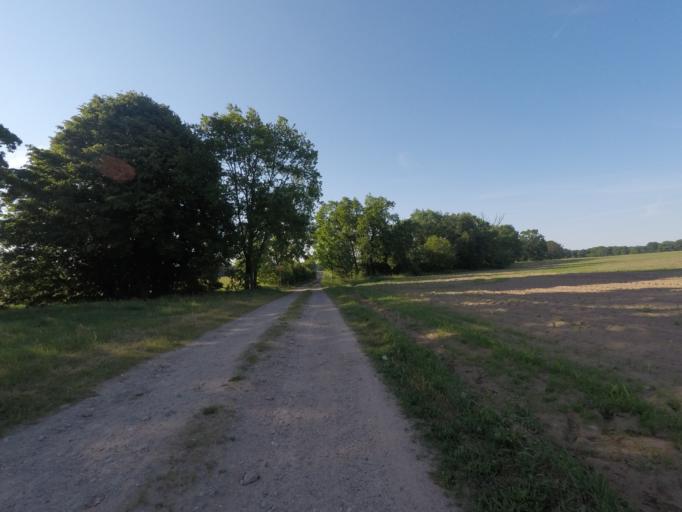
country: DE
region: Brandenburg
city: Joachimsthal
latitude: 52.8954
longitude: 13.7052
